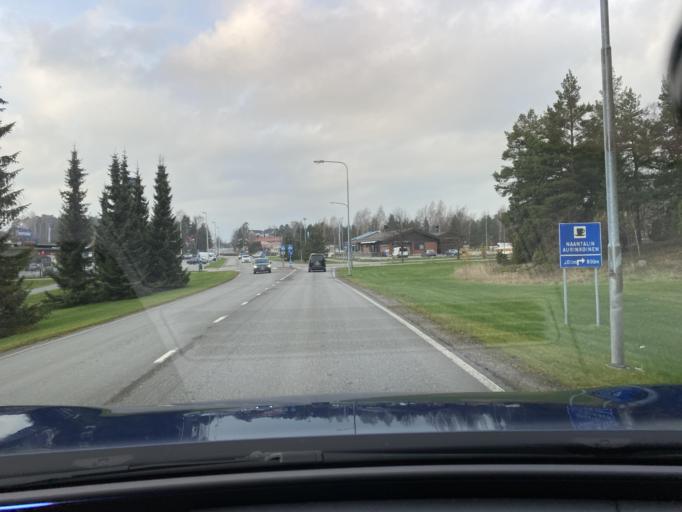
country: FI
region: Varsinais-Suomi
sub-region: Turku
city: Naantali
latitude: 60.4766
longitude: 22.0452
